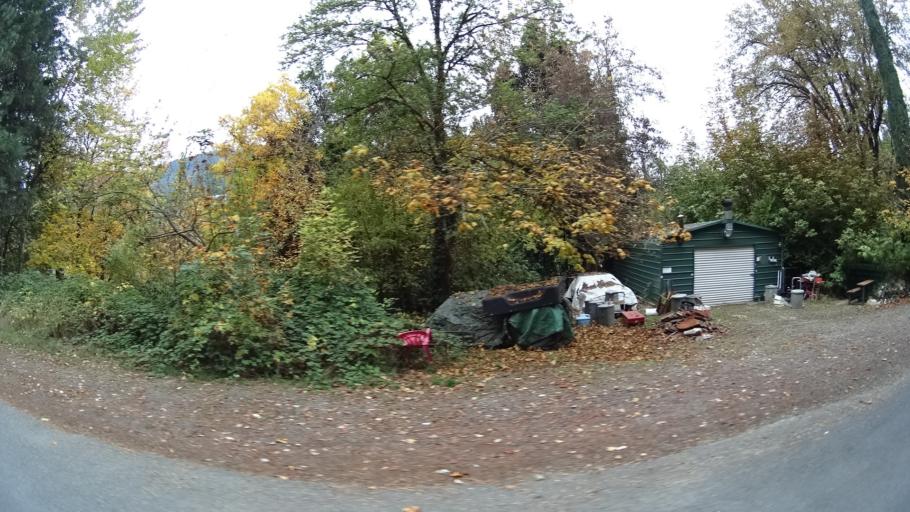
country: US
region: California
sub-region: Siskiyou County
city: Happy Camp
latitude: 41.7895
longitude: -123.3768
